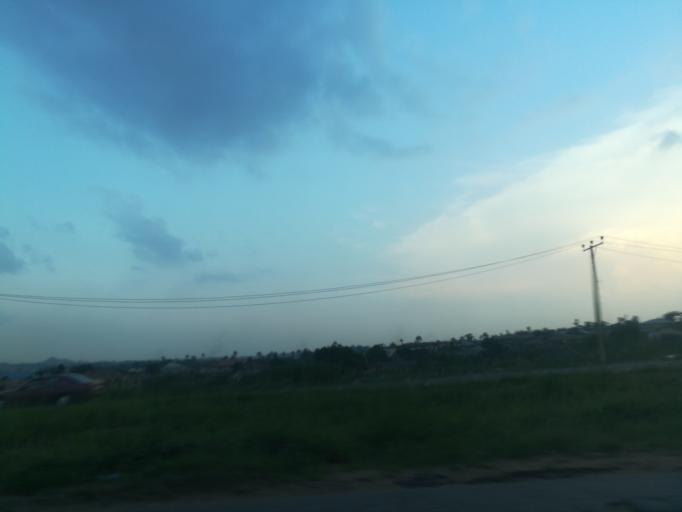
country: NG
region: Oyo
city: Ibadan
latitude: 7.4384
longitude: 3.9280
